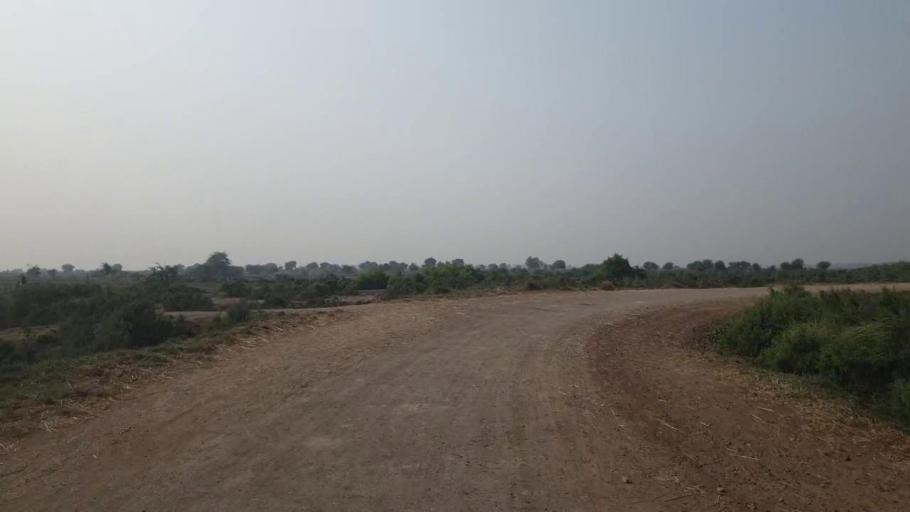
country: PK
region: Sindh
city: Tando Muhammad Khan
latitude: 25.2703
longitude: 68.4838
